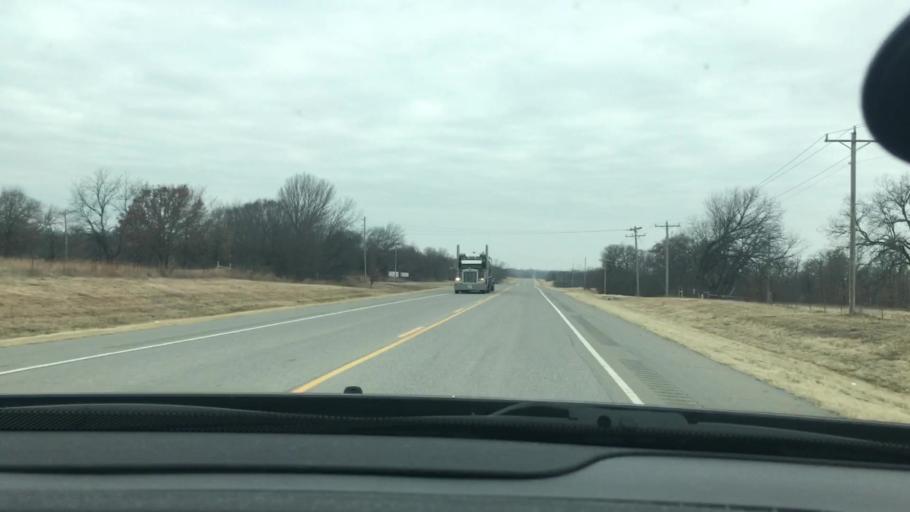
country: US
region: Oklahoma
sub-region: Carter County
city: Healdton
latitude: 34.4924
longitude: -97.4247
